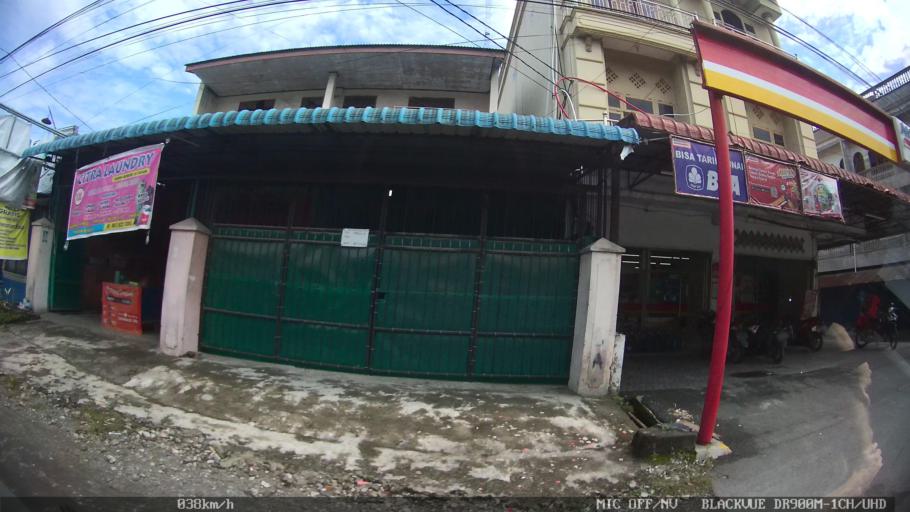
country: ID
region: North Sumatra
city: Medan
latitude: 3.5868
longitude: 98.7296
